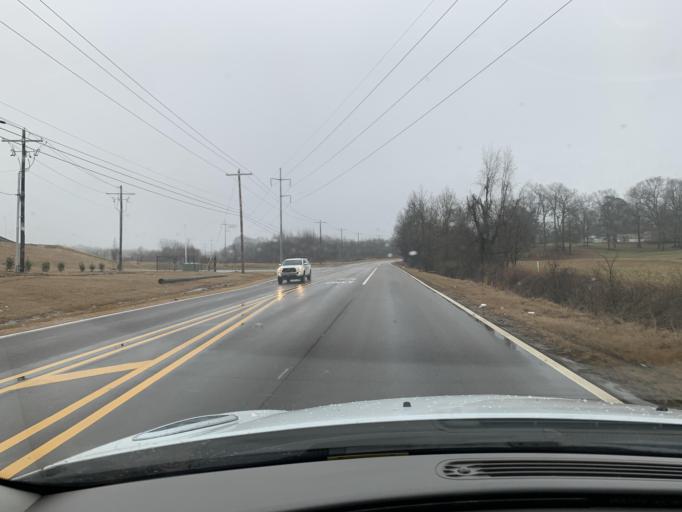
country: US
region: Mississippi
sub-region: De Soto County
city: Horn Lake
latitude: 34.9102
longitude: -90.0008
